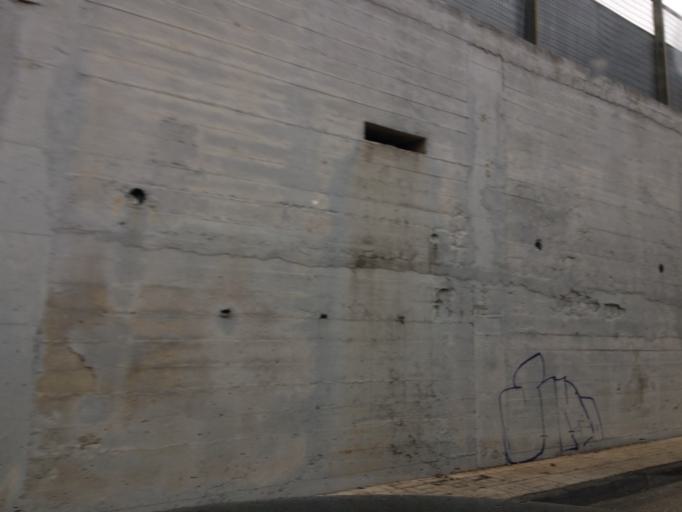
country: ES
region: Andalusia
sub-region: Provincia de Malaga
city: Malaga
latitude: 36.7195
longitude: -4.4451
